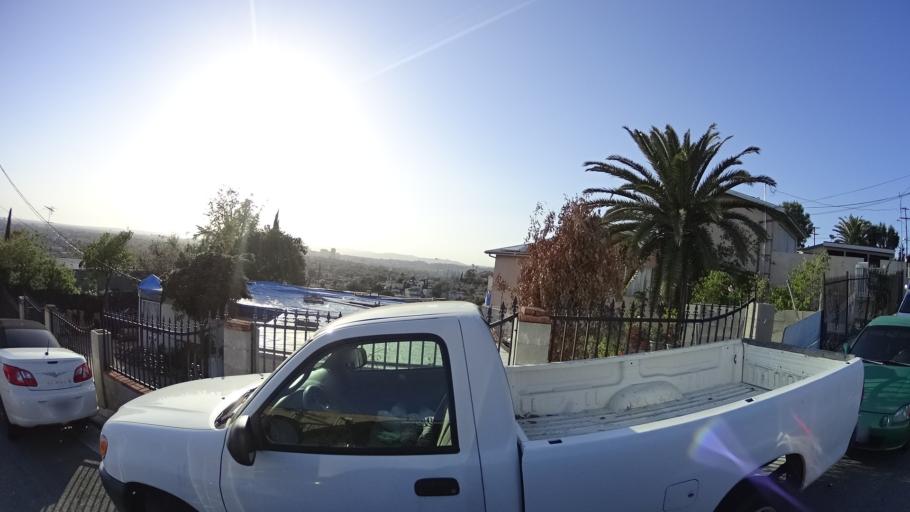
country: US
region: California
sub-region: Los Angeles County
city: Belvedere
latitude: 34.0486
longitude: -118.1864
